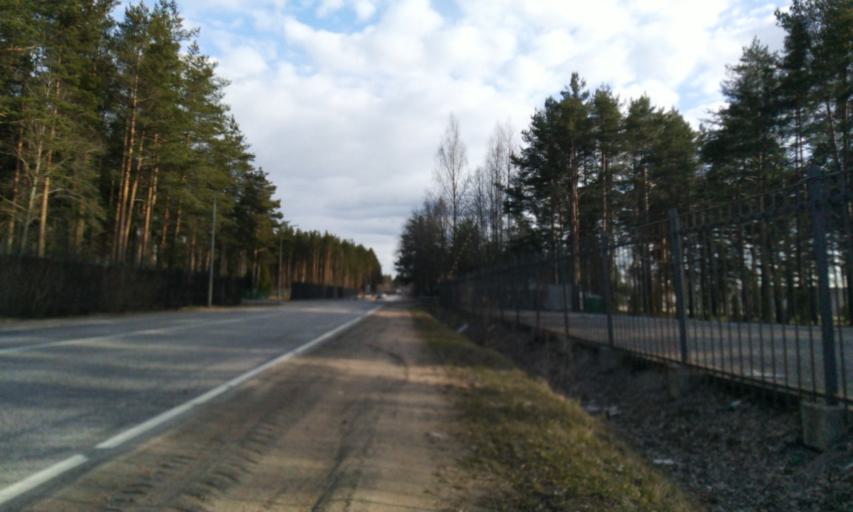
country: RU
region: Leningrad
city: Novoye Devyatkino
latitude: 60.1184
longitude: 30.4489
